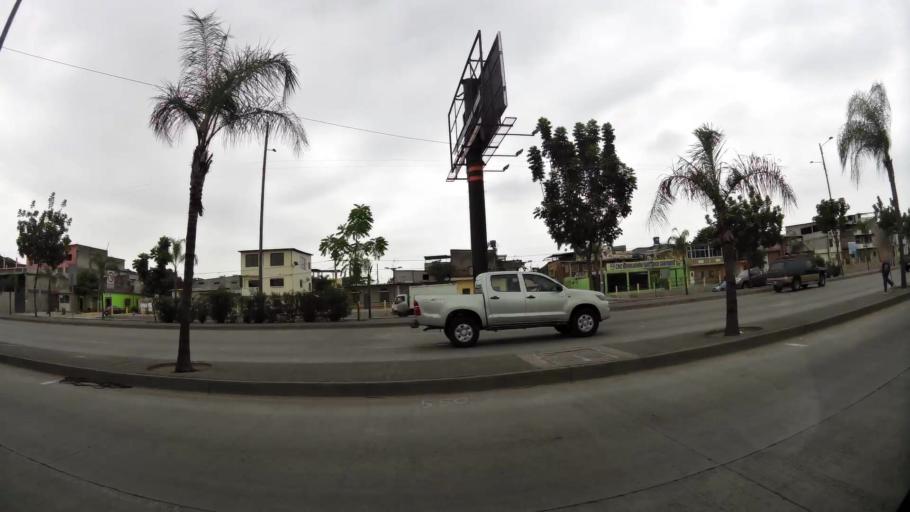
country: EC
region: Guayas
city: Eloy Alfaro
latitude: -2.1244
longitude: -79.8828
